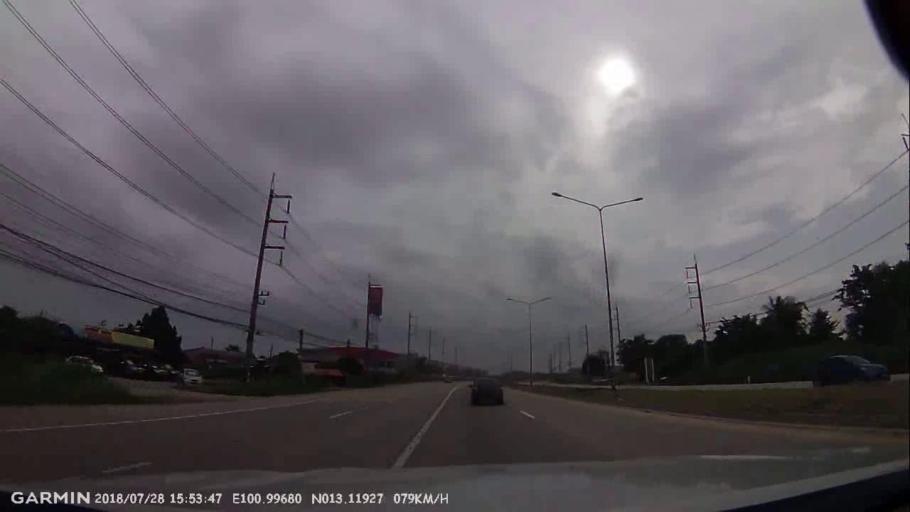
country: TH
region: Chon Buri
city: Ban Talat Bueng
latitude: 13.1192
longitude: 100.9966
